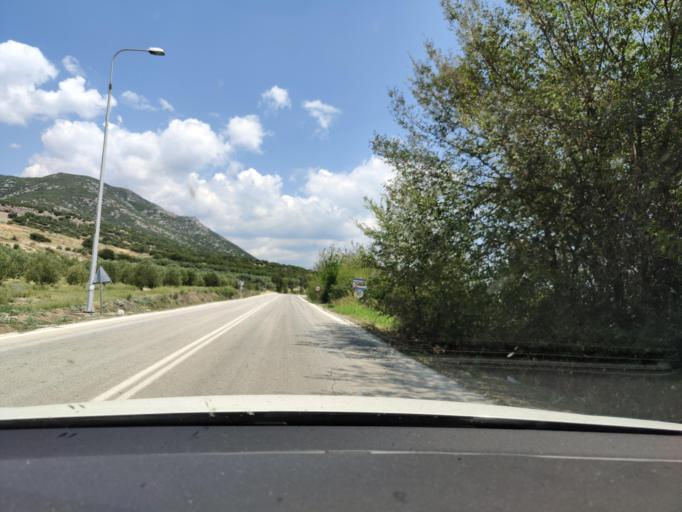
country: GR
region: East Macedonia and Thrace
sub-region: Nomos Kavalas
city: Paralia Ofryniou
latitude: 40.8010
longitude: 23.9532
